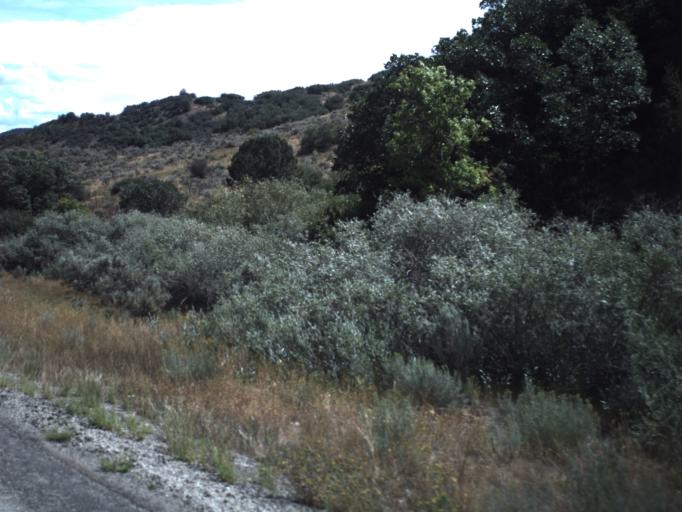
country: US
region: Utah
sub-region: Utah County
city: Woodland Hills
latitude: 39.9601
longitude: -111.5266
